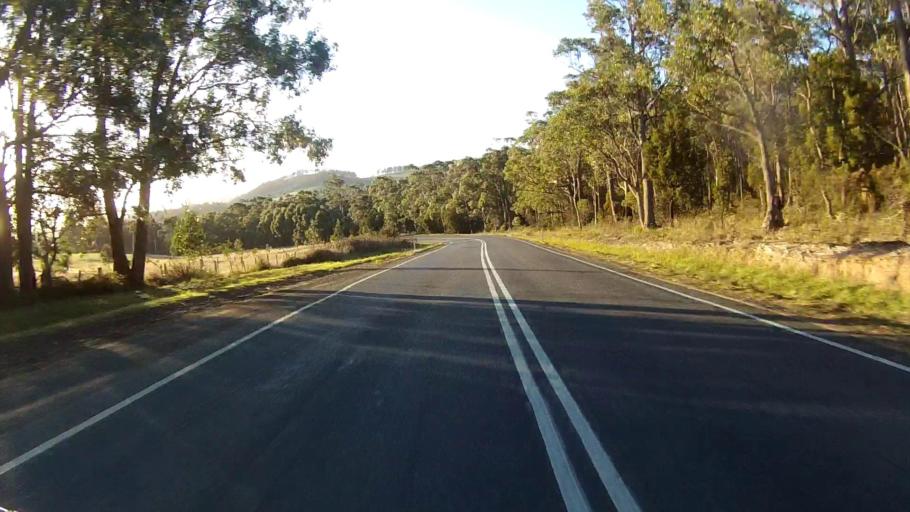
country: AU
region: Tasmania
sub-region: Sorell
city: Sorell
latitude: -42.8284
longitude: 147.8070
